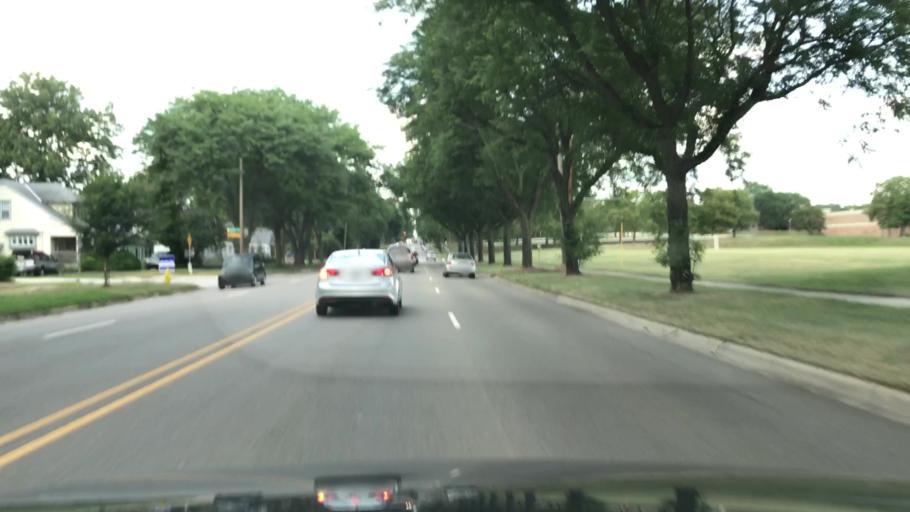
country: US
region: Michigan
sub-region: Kent County
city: Grand Rapids
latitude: 42.9877
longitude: -85.6398
